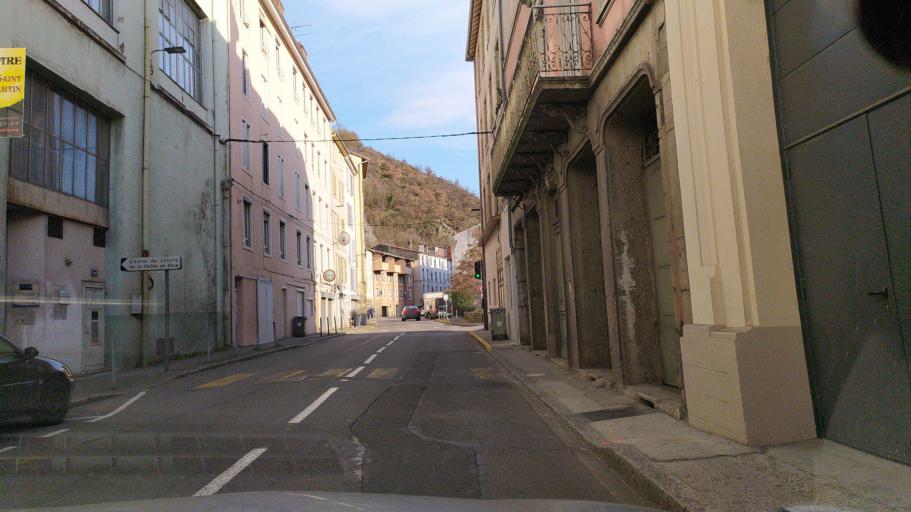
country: FR
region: Rhone-Alpes
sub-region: Departement de l'Isere
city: Vienne
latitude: 45.5273
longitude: 4.8817
